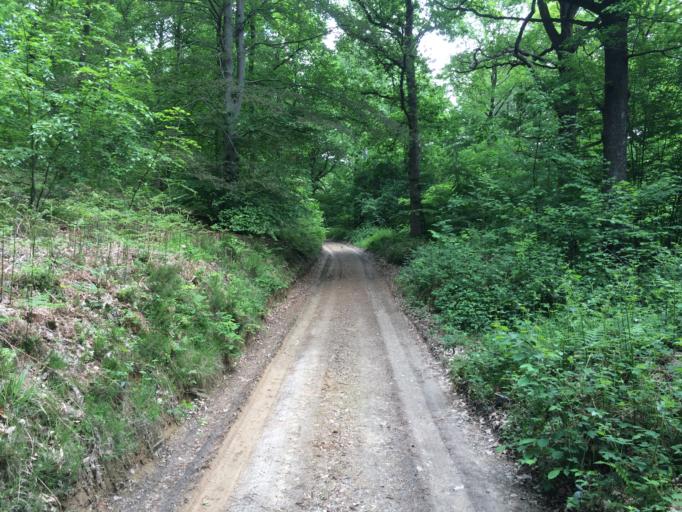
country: BE
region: Wallonia
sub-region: Province de Namur
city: Yvoir
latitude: 50.3341
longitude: 4.9545
